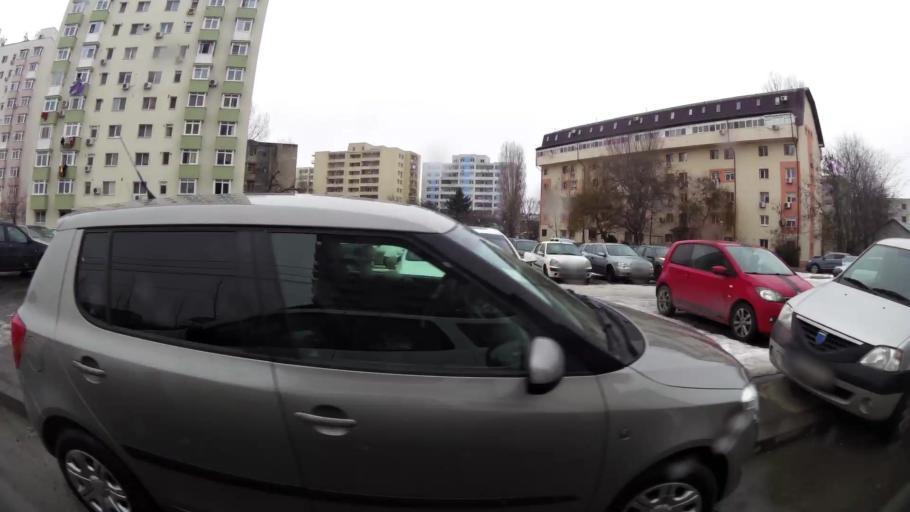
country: RO
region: Ilfov
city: Dobroesti
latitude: 44.4231
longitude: 26.1801
